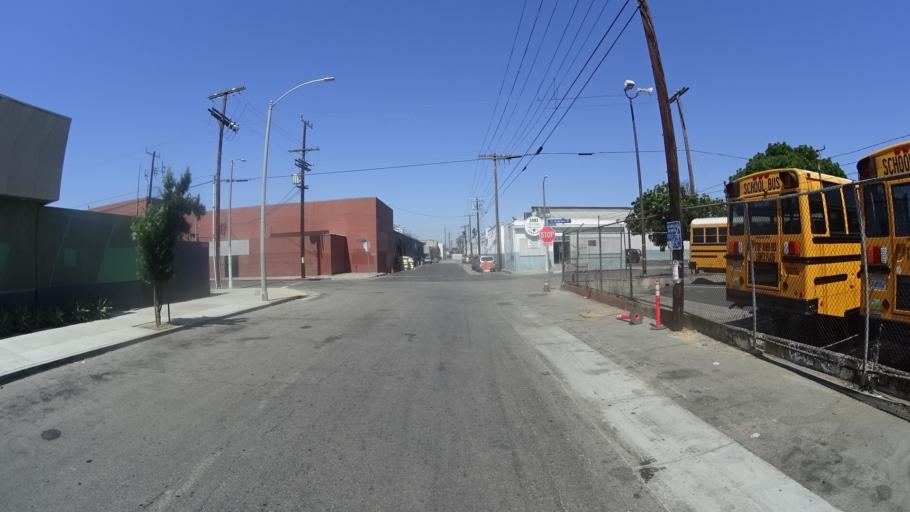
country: US
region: California
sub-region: Los Angeles County
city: View Park-Windsor Hills
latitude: 33.9853
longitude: -118.3112
